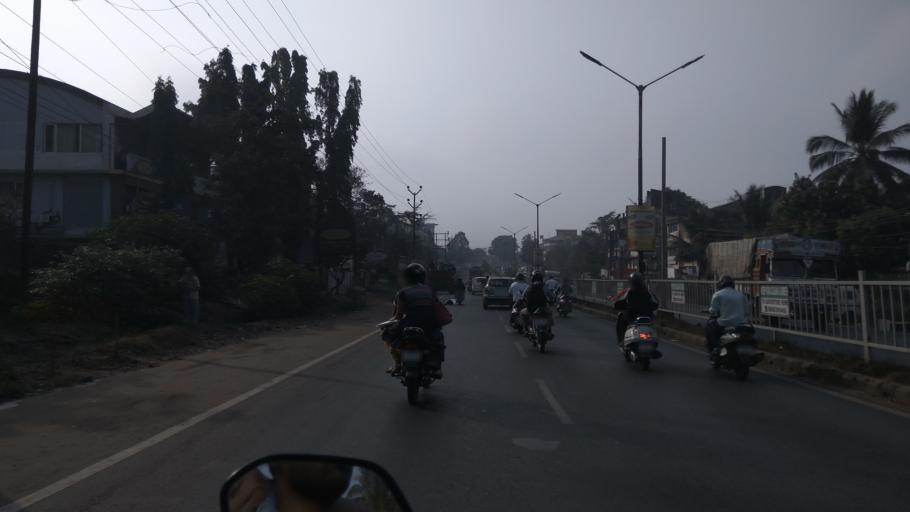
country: IN
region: Goa
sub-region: North Goa
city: Serula
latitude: 15.5296
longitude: 73.8255
